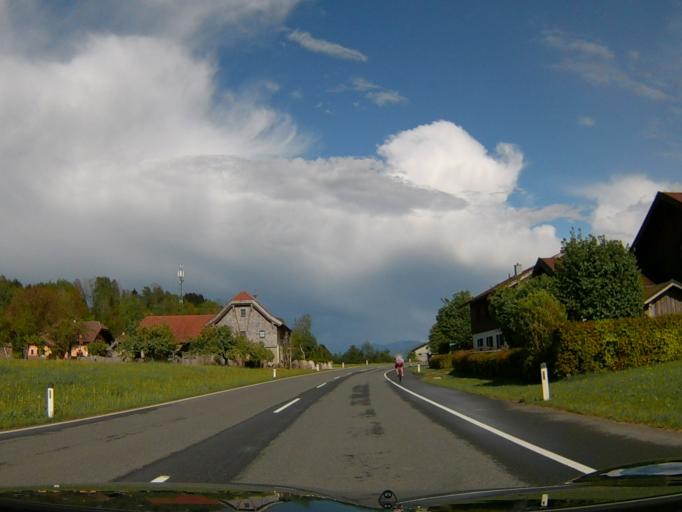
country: AT
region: Salzburg
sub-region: Politischer Bezirk Salzburg-Umgebung
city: Thalgau
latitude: 47.8430
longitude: 13.2635
